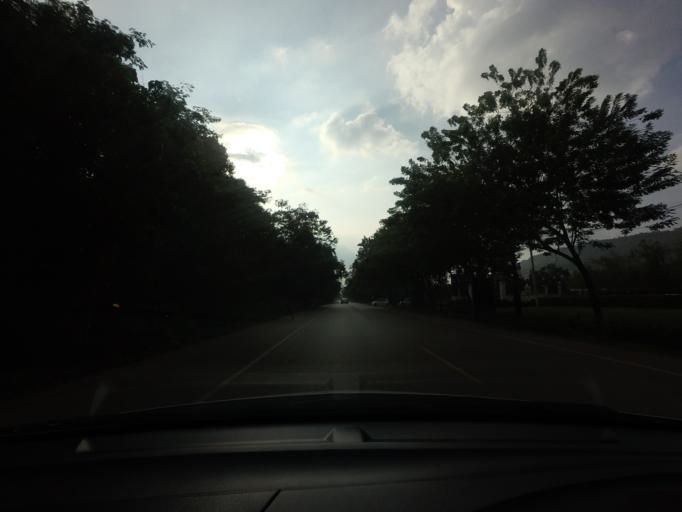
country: TH
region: Nakhon Ratchasima
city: Pak Chong
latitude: 14.5347
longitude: 101.3836
